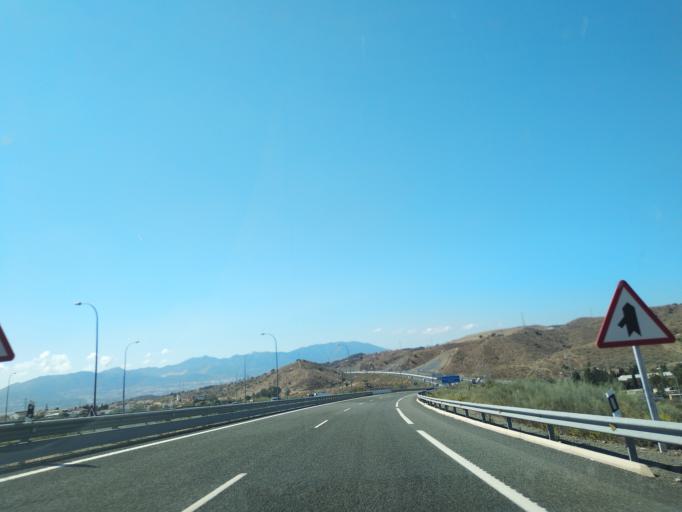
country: ES
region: Andalusia
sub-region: Provincia de Malaga
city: Malaga
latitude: 36.7529
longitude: -4.4903
